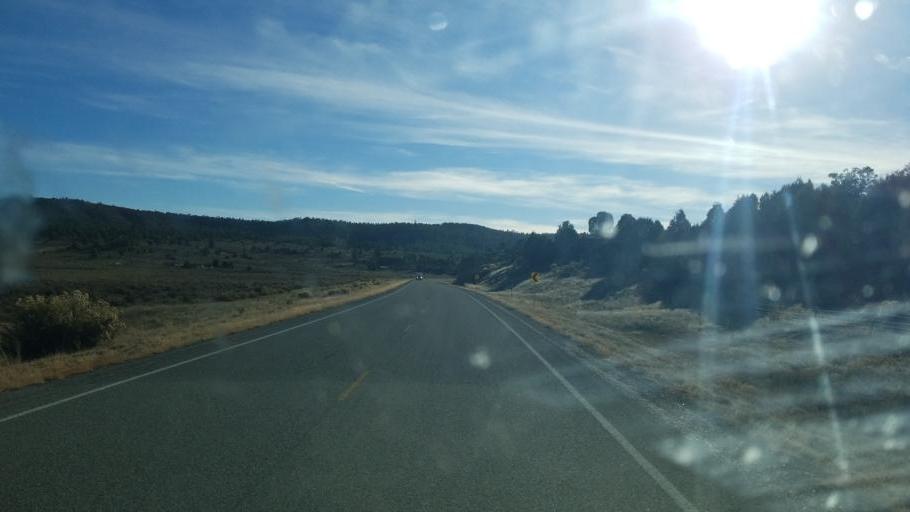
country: US
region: New Mexico
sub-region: Rio Arriba County
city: Navajo
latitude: 36.7507
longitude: -107.2098
